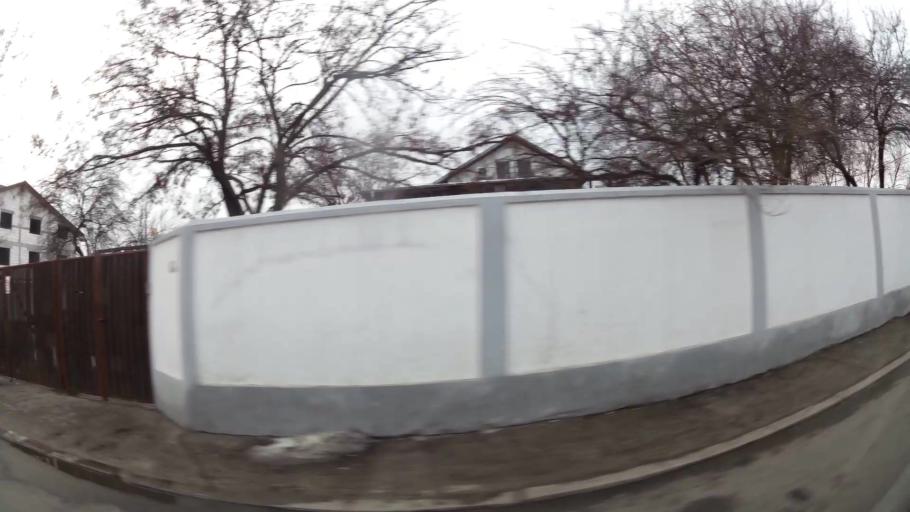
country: RO
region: Ilfov
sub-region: Voluntari City
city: Voluntari
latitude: 44.4941
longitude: 26.1662
